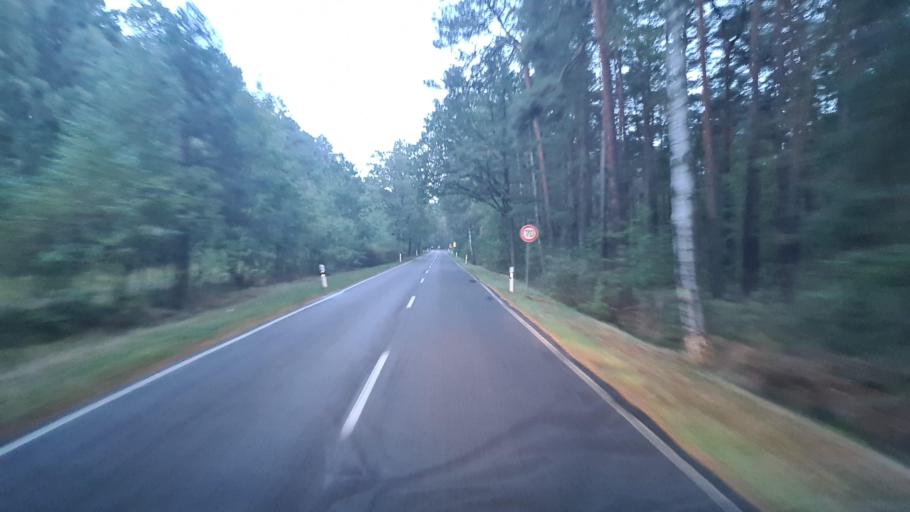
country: DE
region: Brandenburg
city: Schlepzig
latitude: 52.0001
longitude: 13.9270
